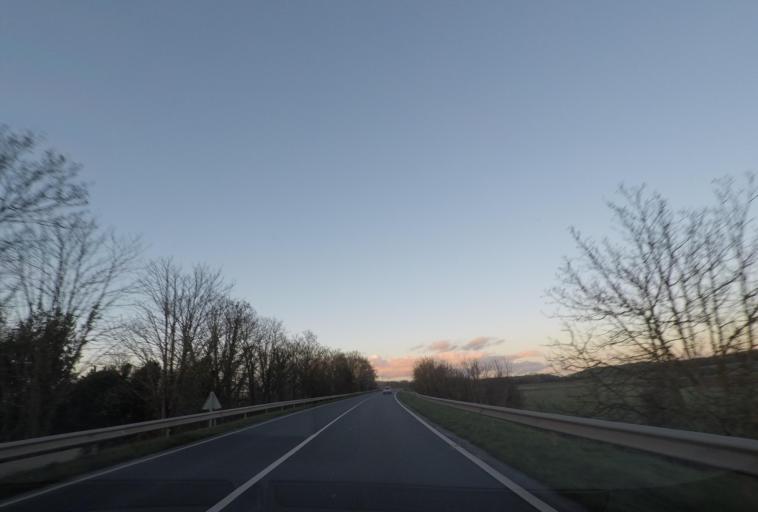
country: FR
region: Ile-de-France
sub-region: Departement de l'Essonne
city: Vert-le-Grand
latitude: 48.5744
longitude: 2.3647
